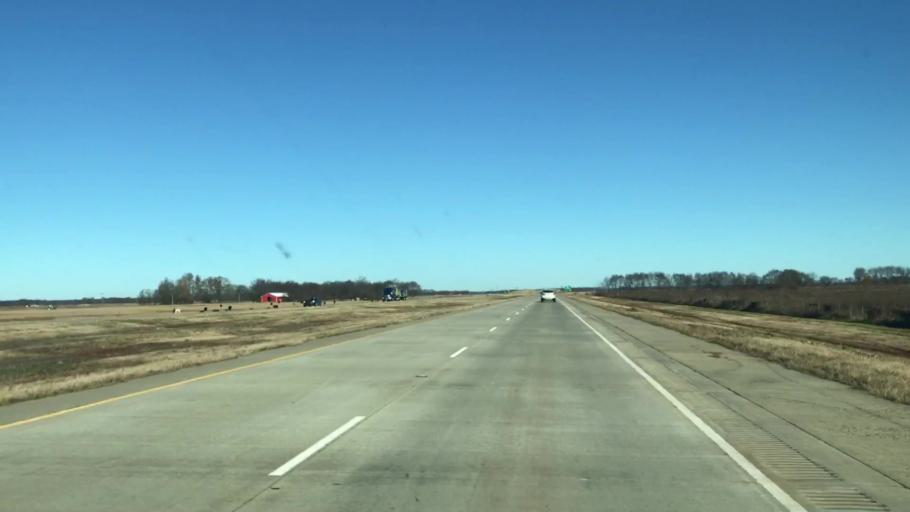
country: US
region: Louisiana
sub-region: Bossier Parish
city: Benton
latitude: 32.6906
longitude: -93.8565
